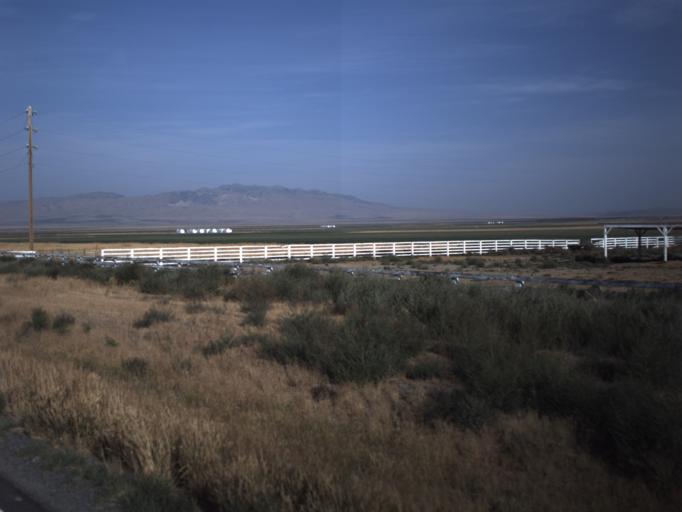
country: US
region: Idaho
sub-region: Oneida County
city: Malad City
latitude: 41.9674
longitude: -112.8058
